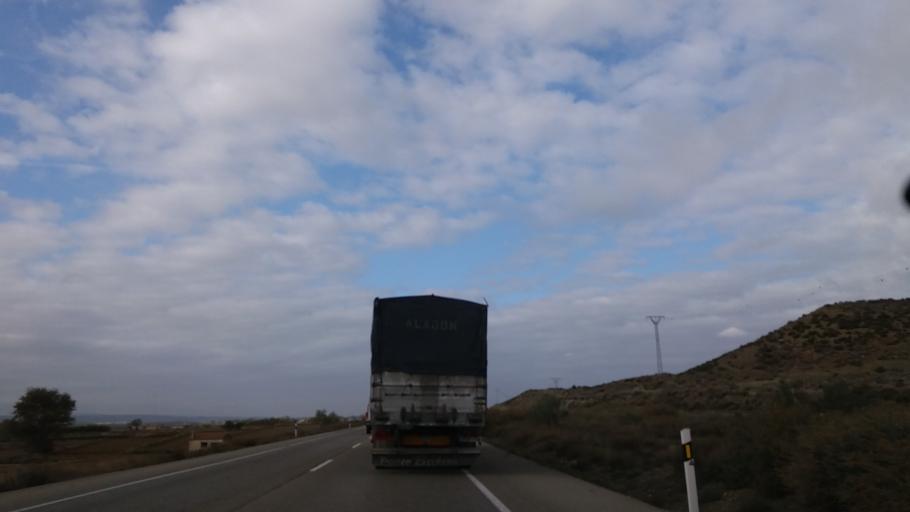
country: ES
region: Aragon
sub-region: Provincia de Zaragoza
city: Pina de Ebro
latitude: 41.5147
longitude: -0.5128
